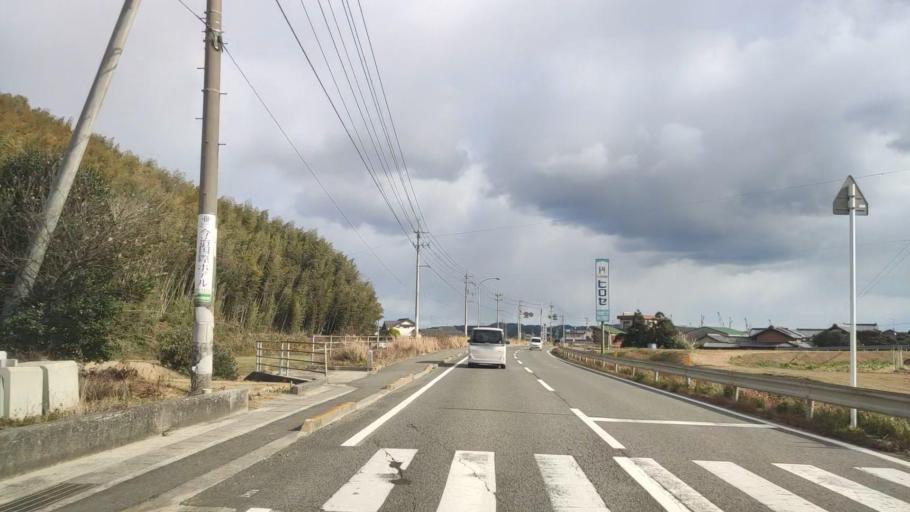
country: JP
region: Ehime
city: Hojo
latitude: 34.0631
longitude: 132.8974
